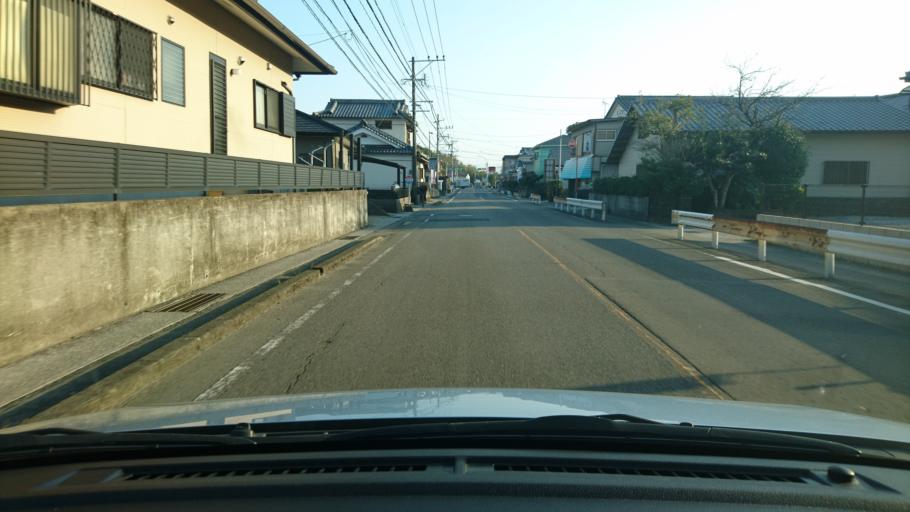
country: JP
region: Miyazaki
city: Miyazaki-shi
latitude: 31.9710
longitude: 131.4398
